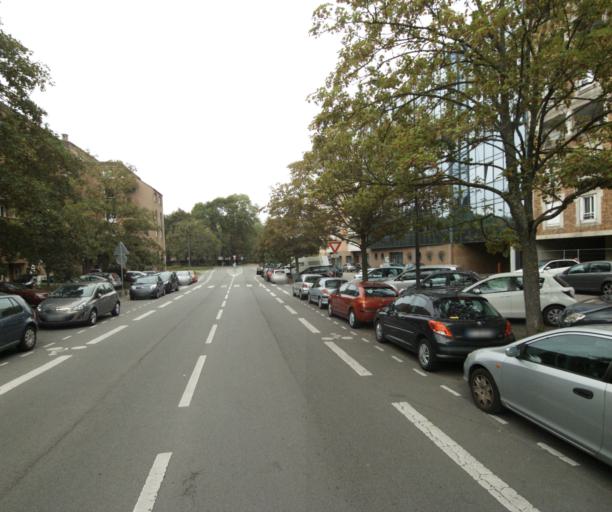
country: FR
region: Nord-Pas-de-Calais
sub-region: Departement du Nord
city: Mons-en-Baroeul
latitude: 50.6226
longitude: 3.1316
